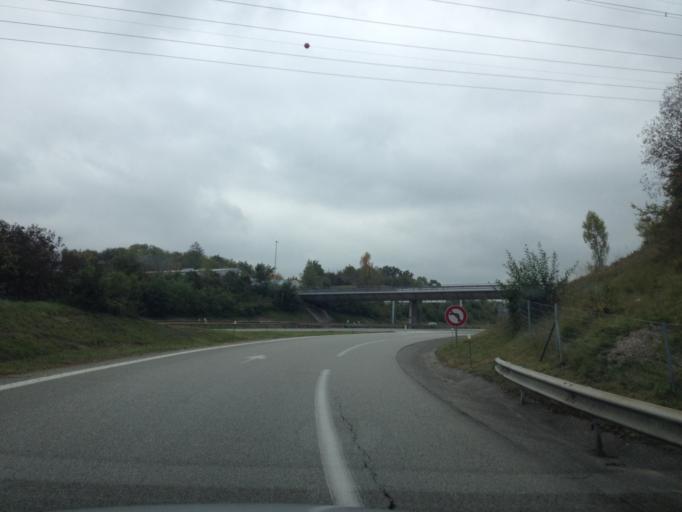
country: FR
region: Rhone-Alpes
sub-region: Departement de la Haute-Savoie
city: Seynod
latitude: 45.8965
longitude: 6.0870
